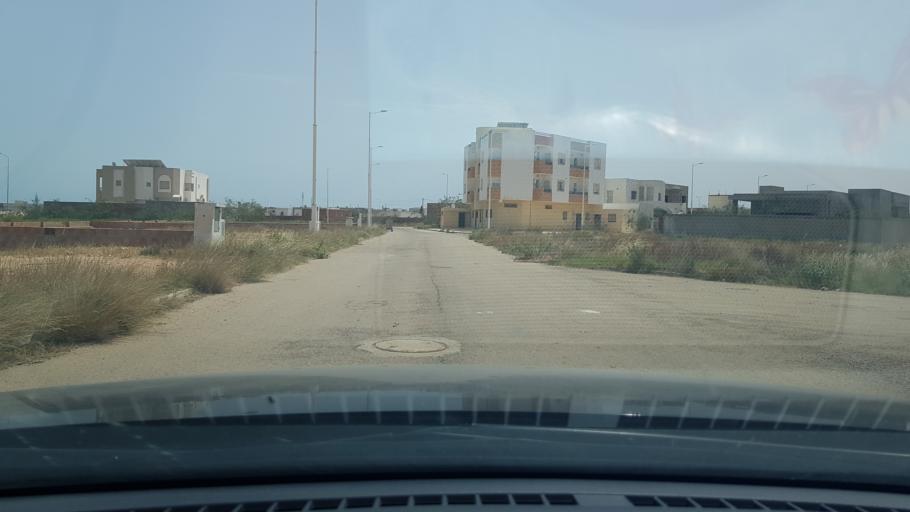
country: TN
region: Safaqis
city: Al Qarmadah
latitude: 34.8323
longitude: 10.7504
